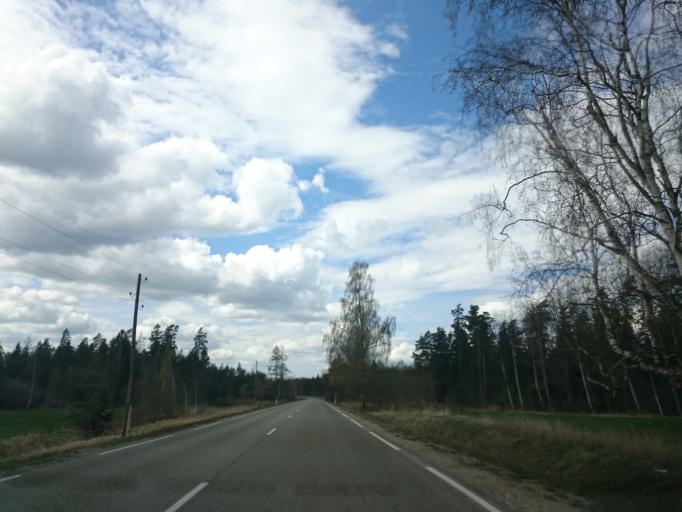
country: LV
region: Talsu Rajons
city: Sabile
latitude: 56.9525
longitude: 22.3028
